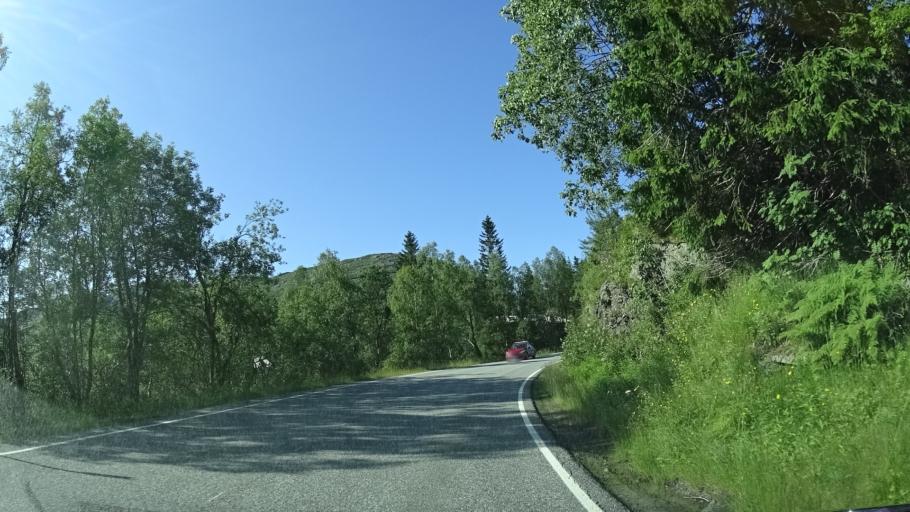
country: NO
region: Hordaland
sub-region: Samnanger
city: Tysse
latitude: 60.3917
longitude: 5.9106
